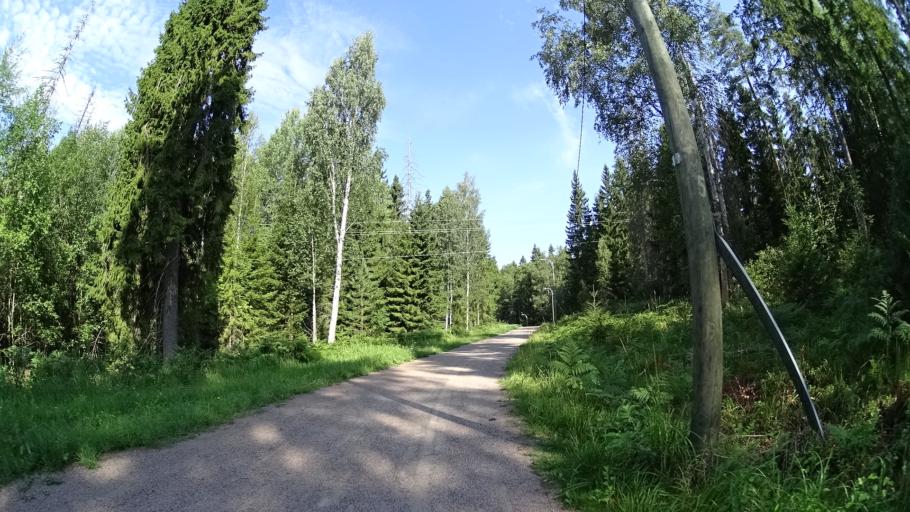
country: FI
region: Uusimaa
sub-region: Helsinki
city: Kilo
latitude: 60.2986
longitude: 24.8150
